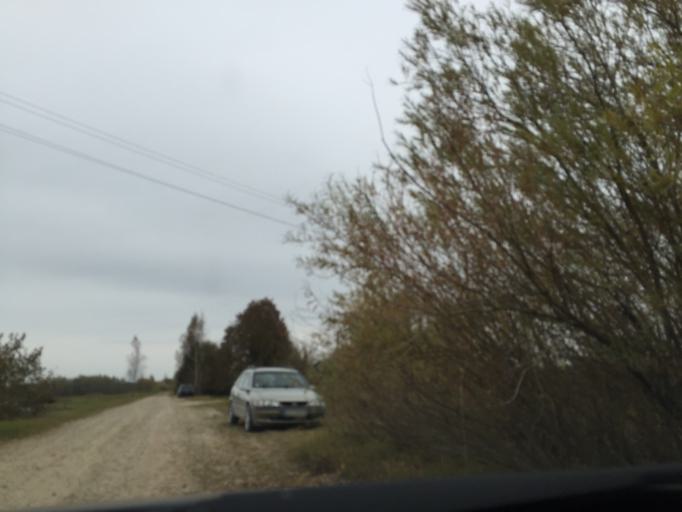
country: LV
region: Ozolnieku
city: Ozolnieki
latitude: 56.6399
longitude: 23.7892
